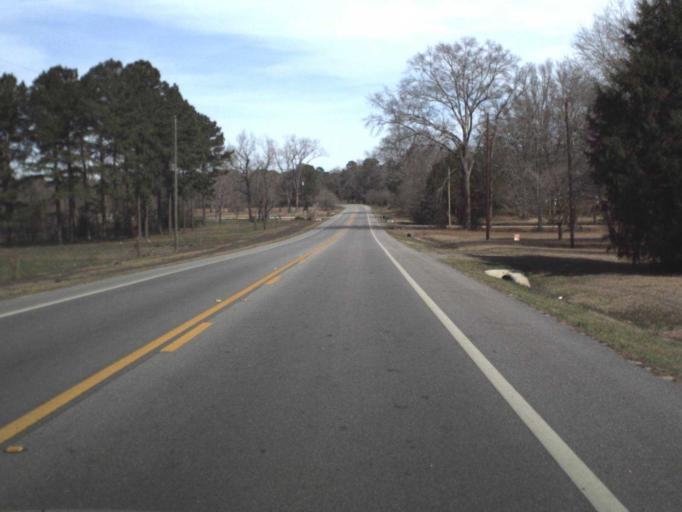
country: US
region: Florida
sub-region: Jackson County
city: Graceville
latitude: 30.9743
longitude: -85.4991
